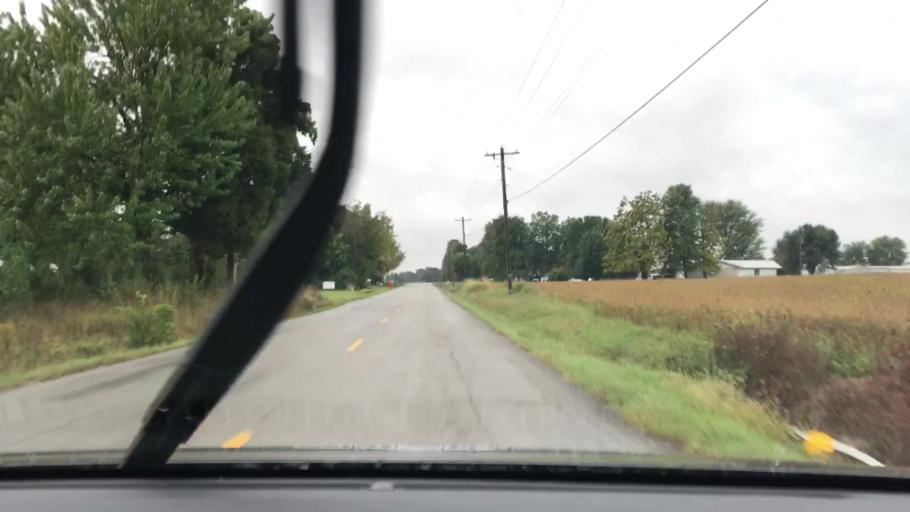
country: US
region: Kentucky
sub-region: McLean County
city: Calhoun
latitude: 37.4403
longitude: -87.2464
